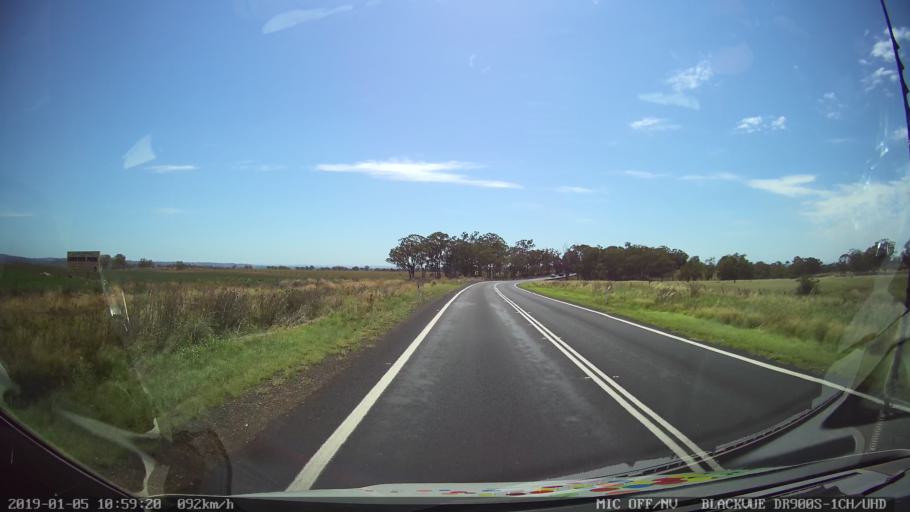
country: AU
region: New South Wales
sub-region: Warrumbungle Shire
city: Coonabarabran
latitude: -31.4156
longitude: 149.1941
